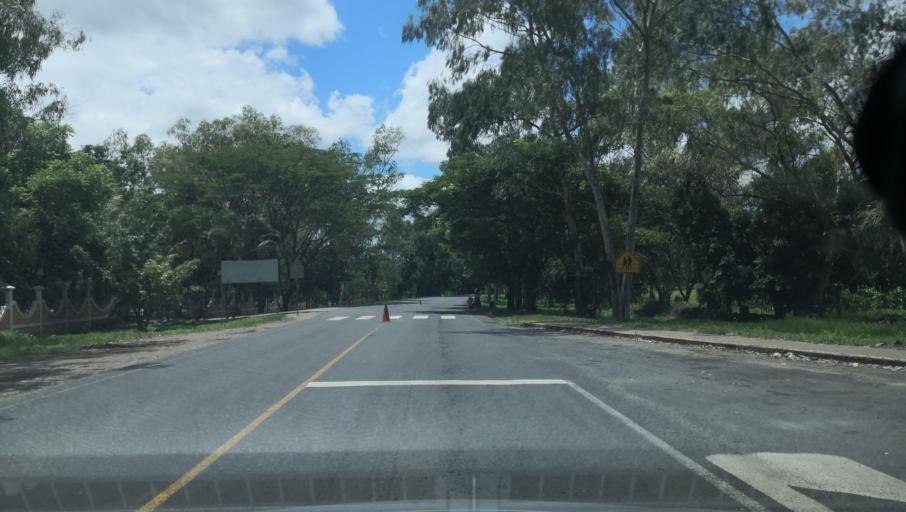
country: NI
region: Esteli
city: Condega
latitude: 13.2459
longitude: -86.3722
